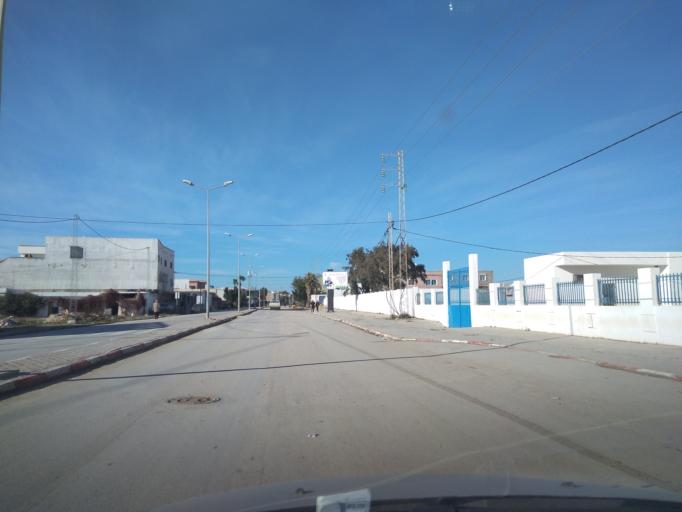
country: TN
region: Ariana
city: Qal'at al Andalus
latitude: 37.0535
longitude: 10.1219
